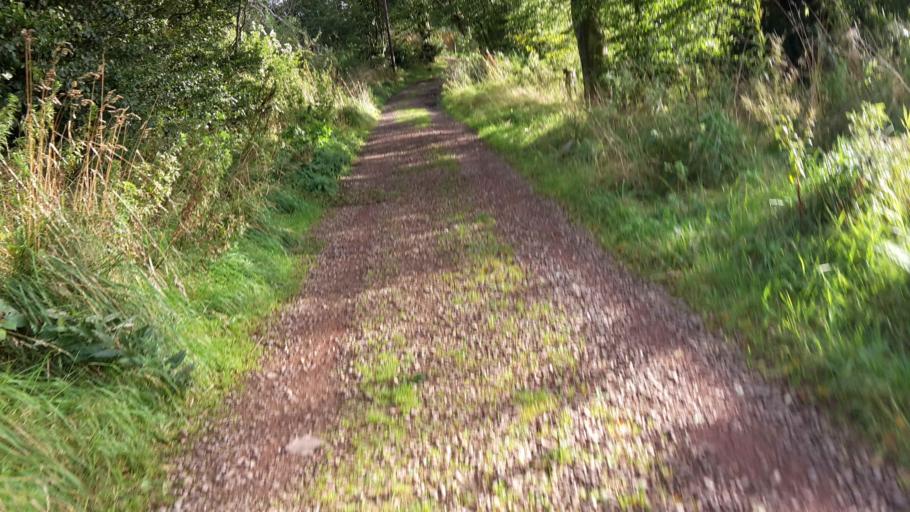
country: GB
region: Scotland
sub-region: South Lanarkshire
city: Carluke
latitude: 55.7235
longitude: -3.8282
